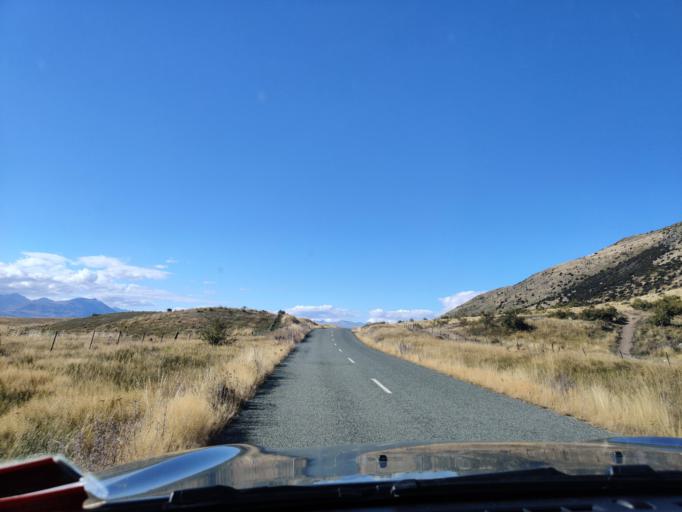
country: NZ
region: Canterbury
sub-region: Timaru District
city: Pleasant Point
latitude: -43.9831
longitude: 170.4577
